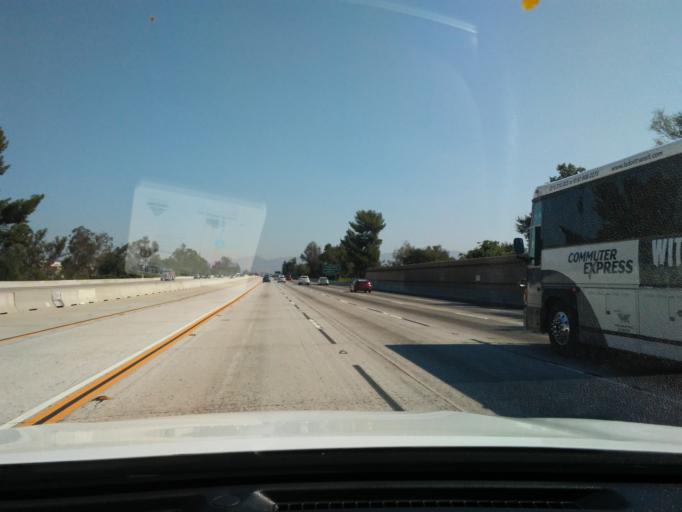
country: US
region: California
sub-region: Los Angeles County
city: Van Nuys
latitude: 34.2117
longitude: -118.4732
